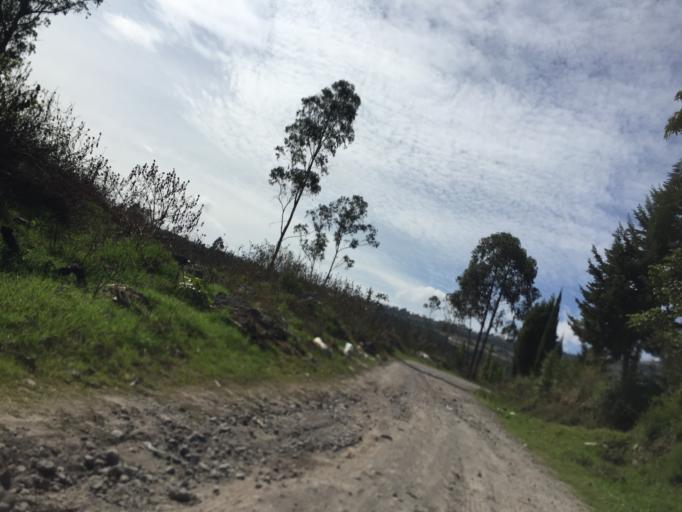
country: EC
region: Imbabura
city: Ibarra
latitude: 0.3154
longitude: -78.1477
